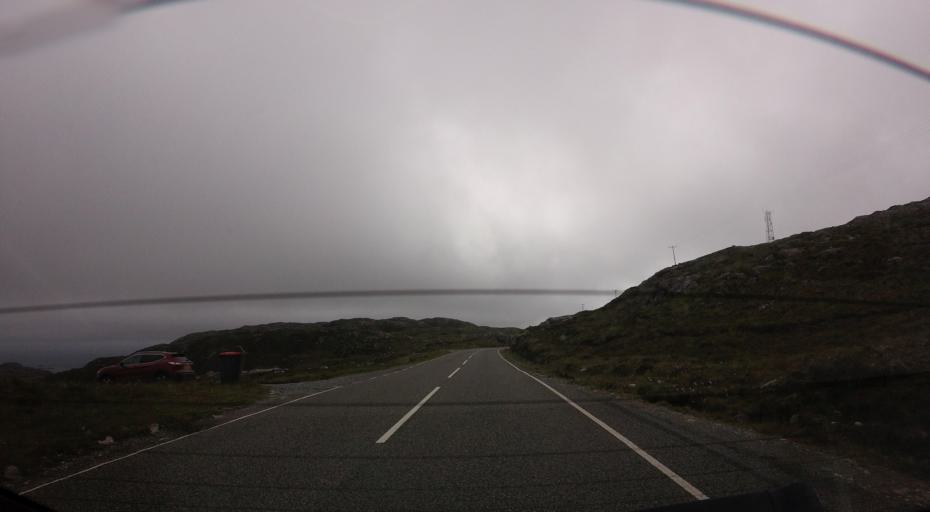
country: GB
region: Scotland
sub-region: Eilean Siar
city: Harris
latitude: 57.8507
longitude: -6.8211
